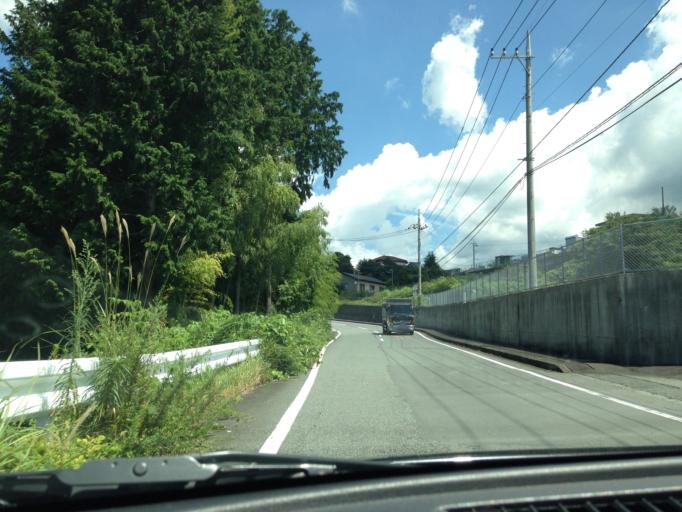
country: JP
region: Shizuoka
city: Fuji
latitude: 35.1967
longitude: 138.7152
